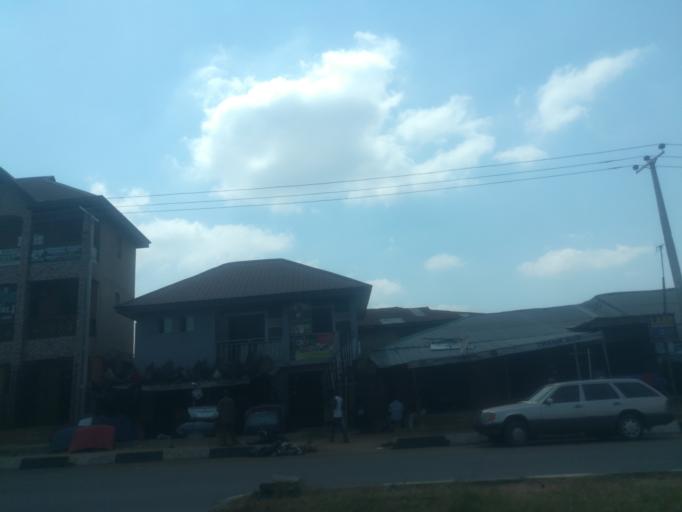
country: NG
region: Ogun
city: Abeokuta
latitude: 7.1525
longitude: 3.3506
